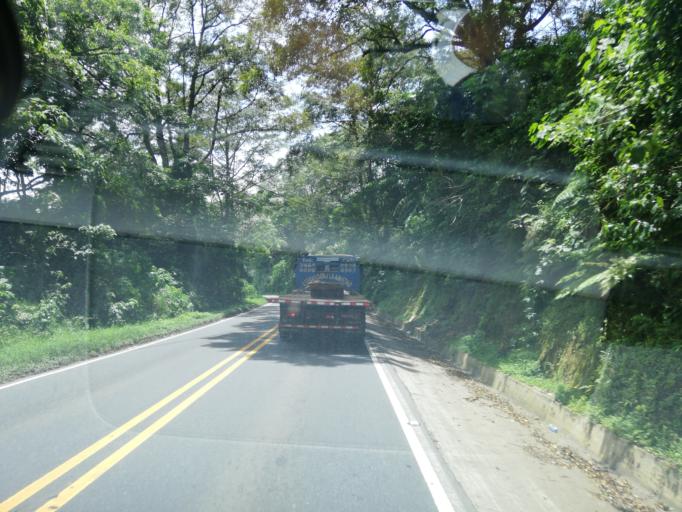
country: CR
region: Alajuela
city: Zarcero
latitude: 10.2235
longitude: -84.4079
